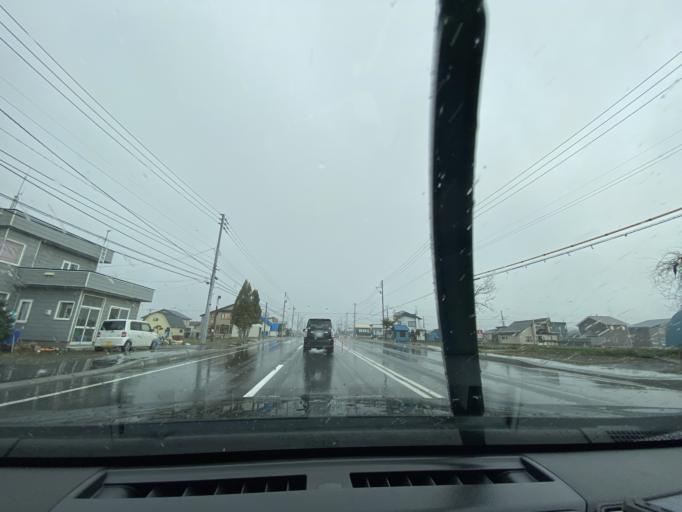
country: JP
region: Hokkaido
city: Takikawa
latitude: 43.6183
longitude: 141.9376
